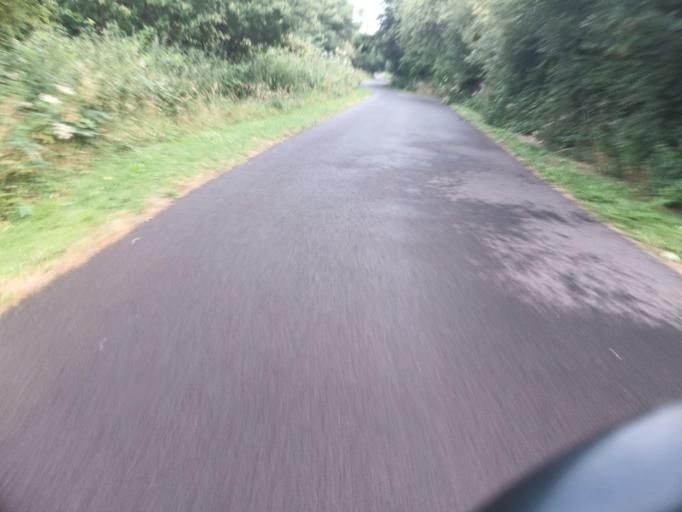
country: GB
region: Northern Ireland
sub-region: Castlereagh District
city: Dundonald
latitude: 54.5792
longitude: -5.7863
